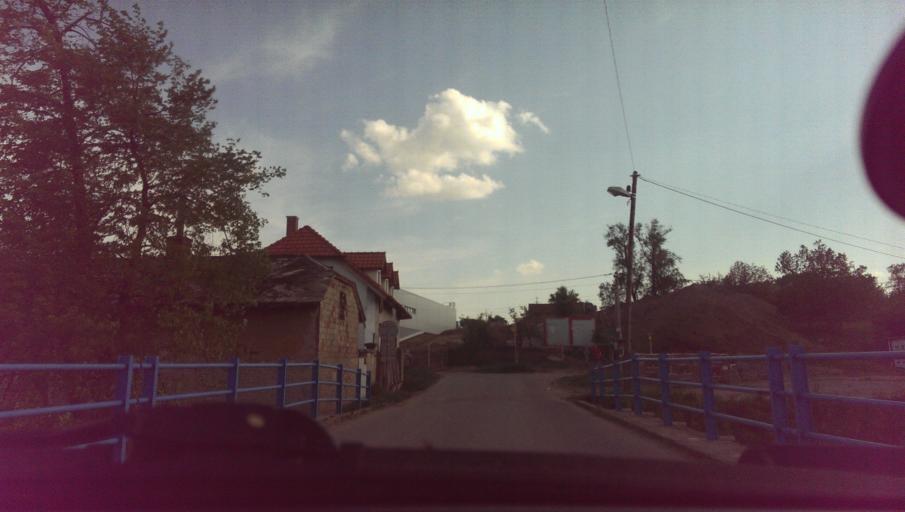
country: CZ
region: Zlin
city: Uhersky Brod
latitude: 49.0163
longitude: 17.6442
